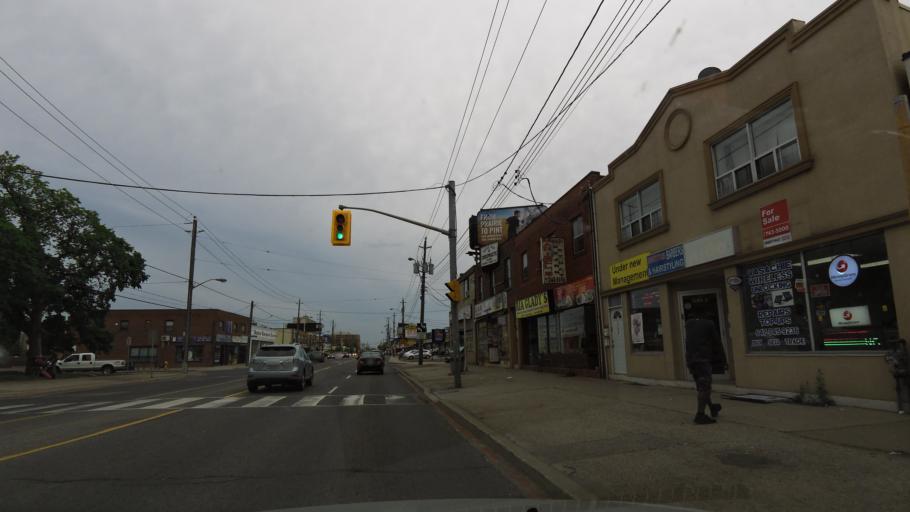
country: CA
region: Ontario
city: Etobicoke
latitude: 43.7050
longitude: -79.5045
